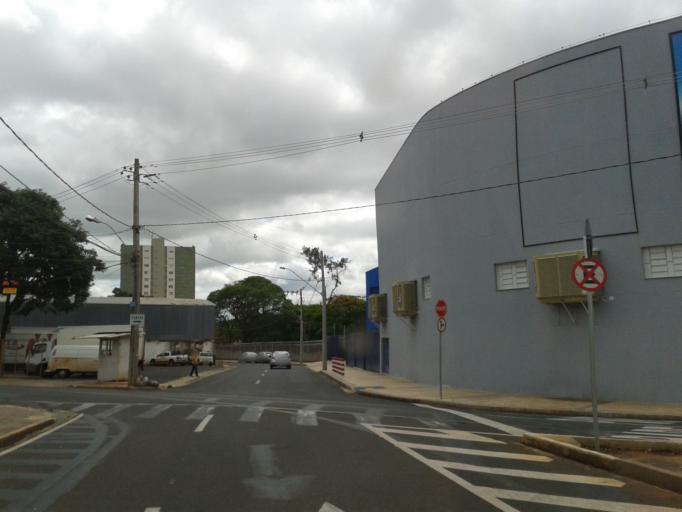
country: BR
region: Minas Gerais
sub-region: Uberaba
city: Uberaba
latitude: -19.7485
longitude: -47.9482
